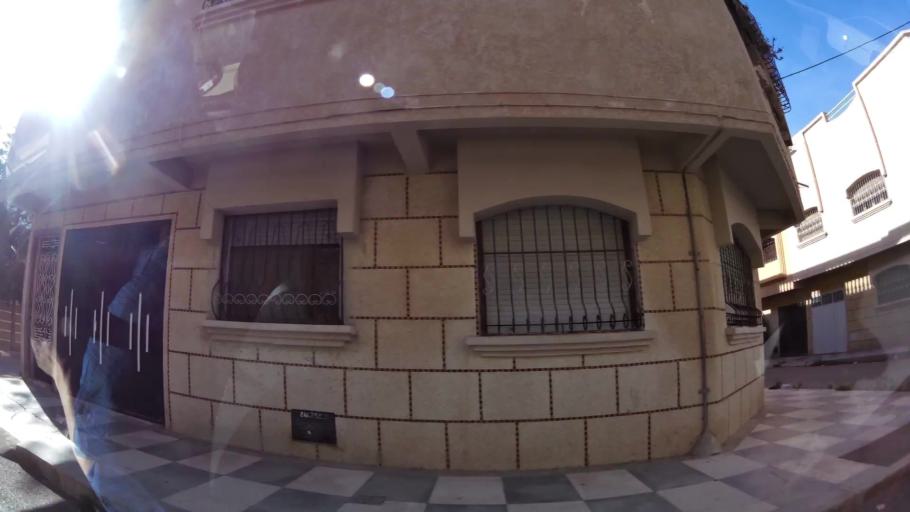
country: MA
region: Oriental
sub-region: Oujda-Angad
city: Oujda
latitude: 34.6661
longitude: -1.8987
